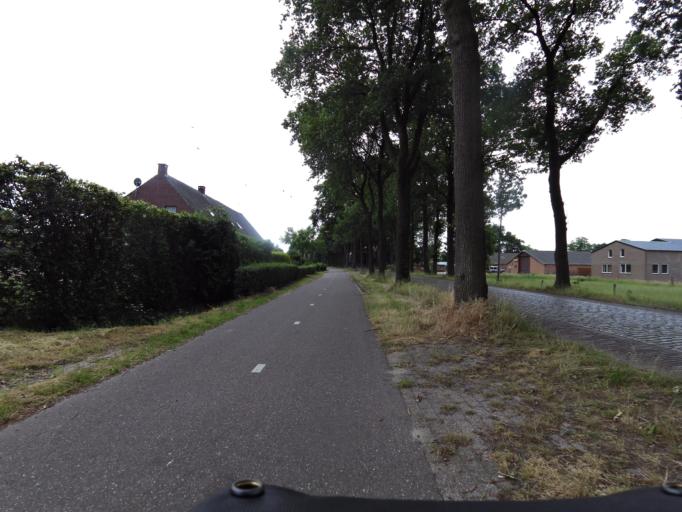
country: NL
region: North Brabant
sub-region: Gemeente Bladel en Netersel
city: Bladel
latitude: 51.3830
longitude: 5.2125
